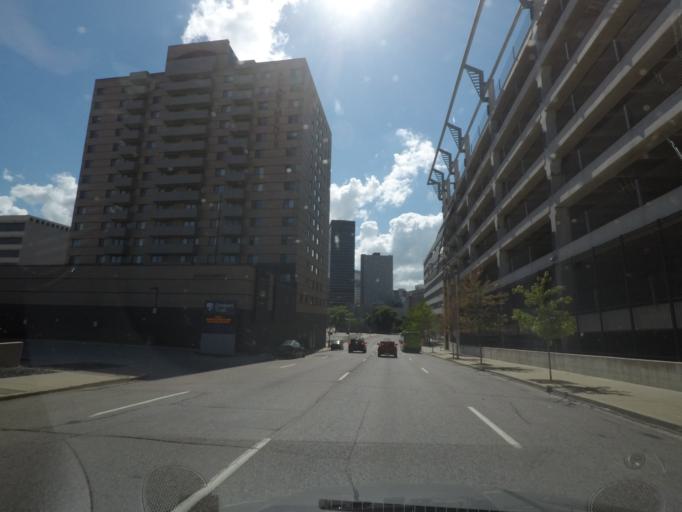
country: US
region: Iowa
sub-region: Polk County
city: Des Moines
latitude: 41.5912
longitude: -93.6269
